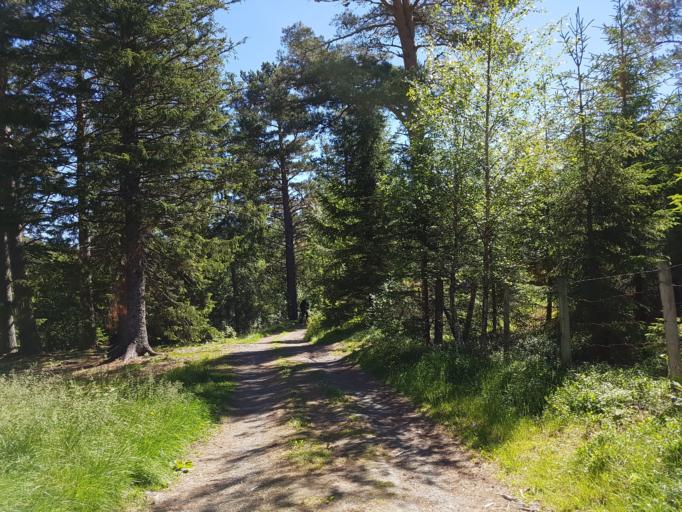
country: NO
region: Sor-Trondelag
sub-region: Skaun
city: Borsa
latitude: 63.4318
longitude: 10.1868
